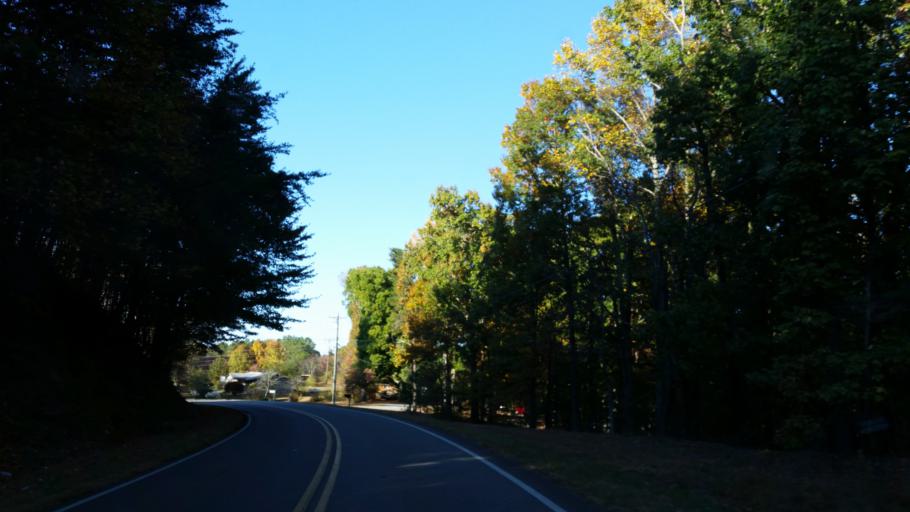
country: US
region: Georgia
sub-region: Gilmer County
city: Ellijay
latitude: 34.5917
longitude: -84.4578
